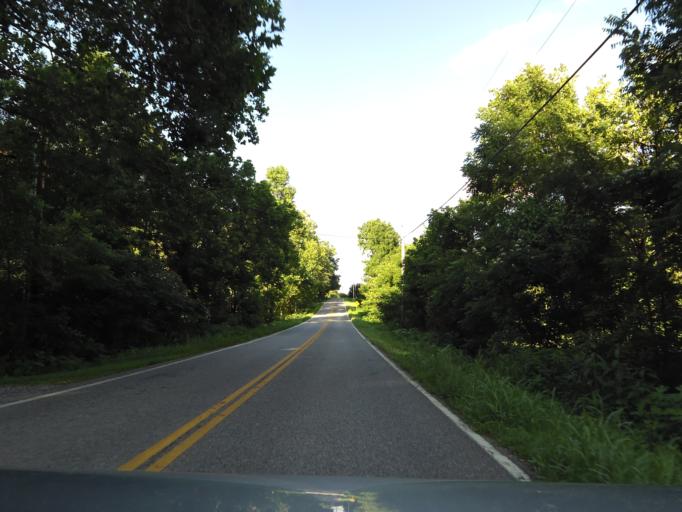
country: US
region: Tennessee
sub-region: Blount County
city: Maryville
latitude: 35.6499
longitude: -83.9796
